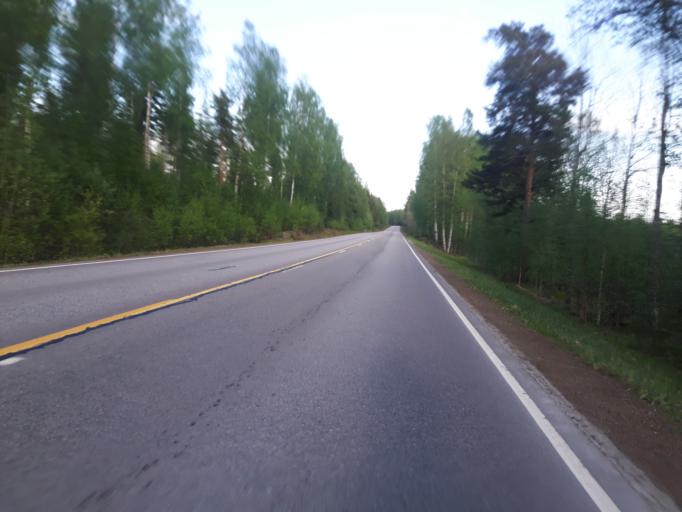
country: FI
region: Uusimaa
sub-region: Loviisa
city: Perna
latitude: 60.4605
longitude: 26.0478
